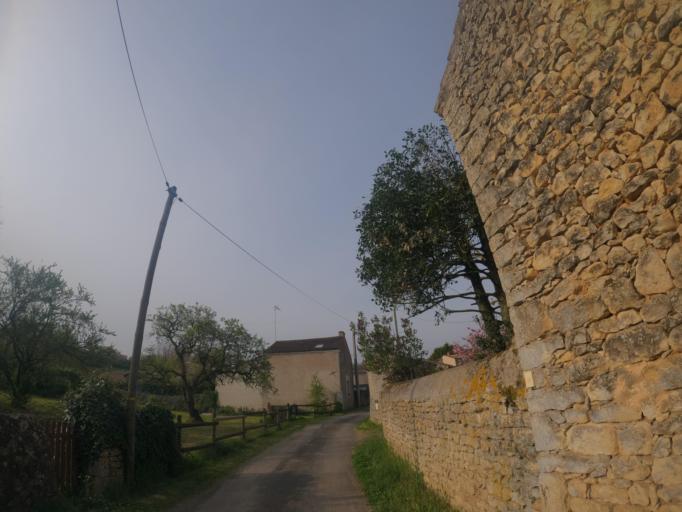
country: FR
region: Poitou-Charentes
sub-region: Departement des Deux-Sevres
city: Saint-Jean-de-Thouars
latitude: 46.9211
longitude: -0.1798
